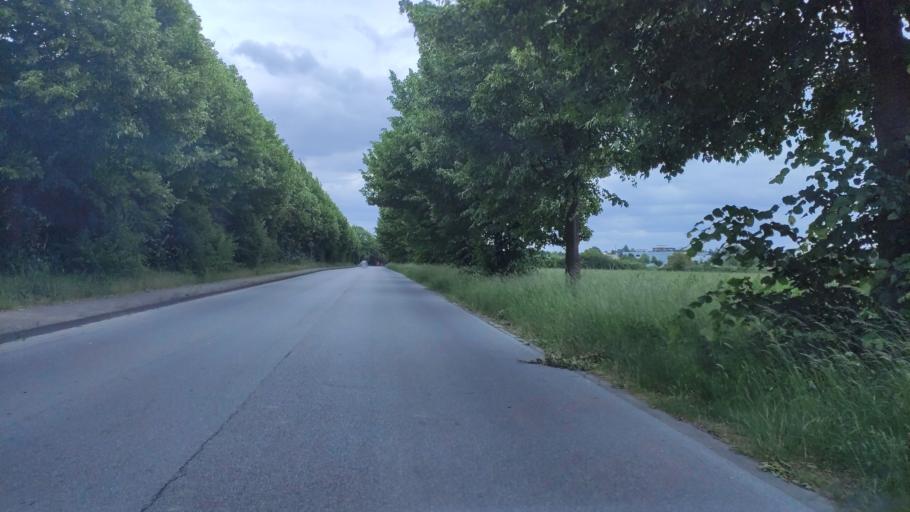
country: DE
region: North Rhine-Westphalia
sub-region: Regierungsbezirk Dusseldorf
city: Neubrueck
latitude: 51.1665
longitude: 6.6571
